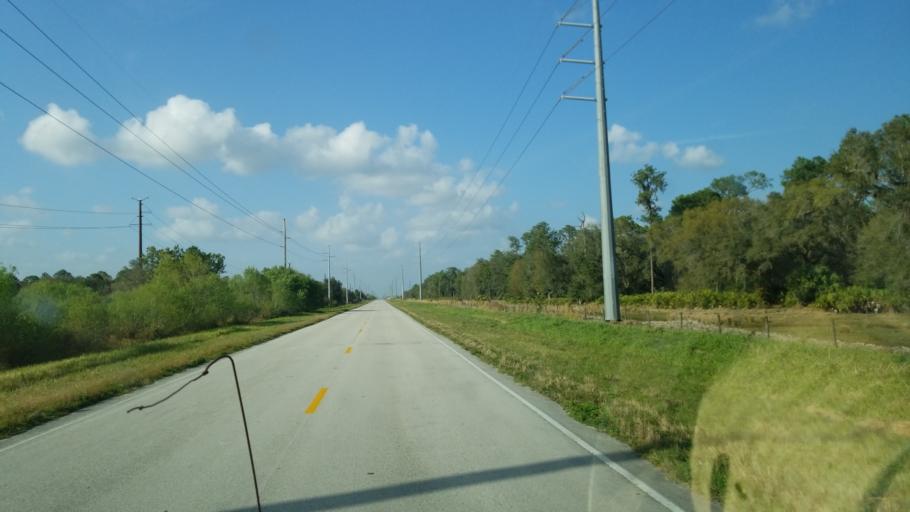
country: US
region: Florida
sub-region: Hardee County
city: Wauchula
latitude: 27.5097
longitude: -81.9243
